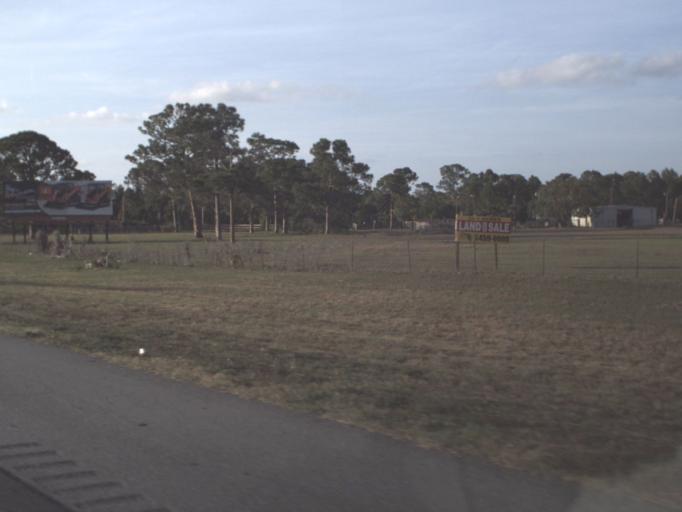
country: US
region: Florida
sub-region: Brevard County
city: Port Saint John
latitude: 28.4840
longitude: -80.8243
